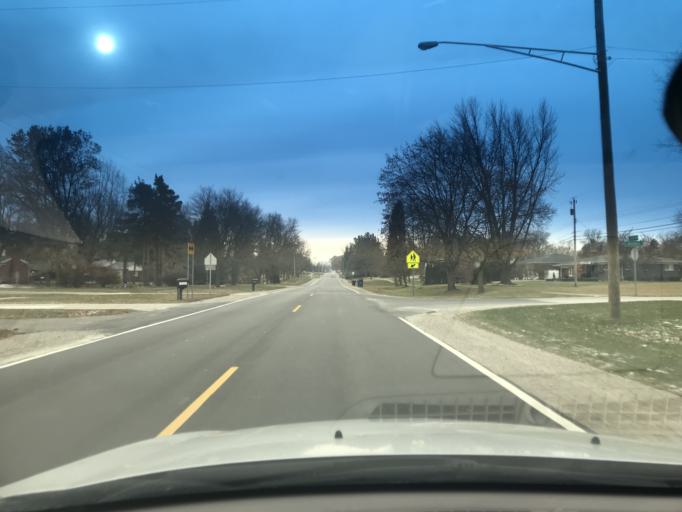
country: US
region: Michigan
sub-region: Macomb County
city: Shelby
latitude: 42.6933
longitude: -83.0544
